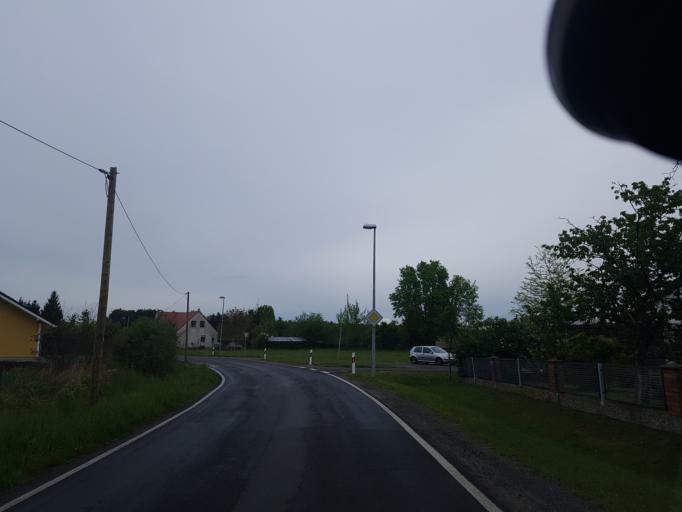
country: DE
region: Brandenburg
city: Spremberg
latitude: 51.6726
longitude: 14.4410
